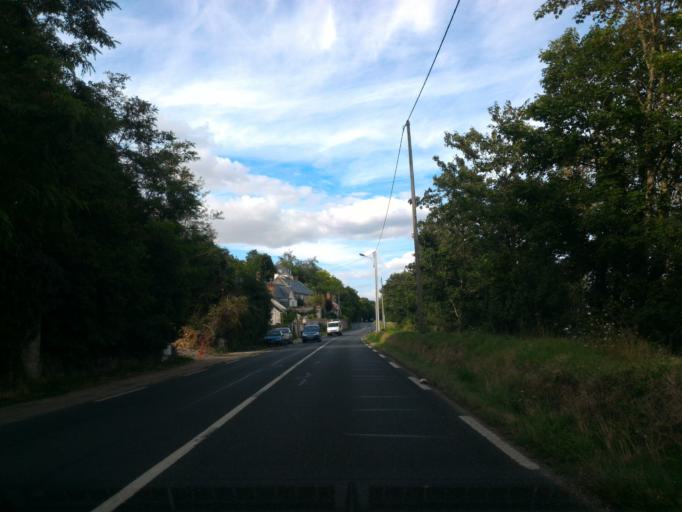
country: FR
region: Centre
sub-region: Departement du Loir-et-Cher
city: Chailles
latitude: 47.5641
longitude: 1.3018
